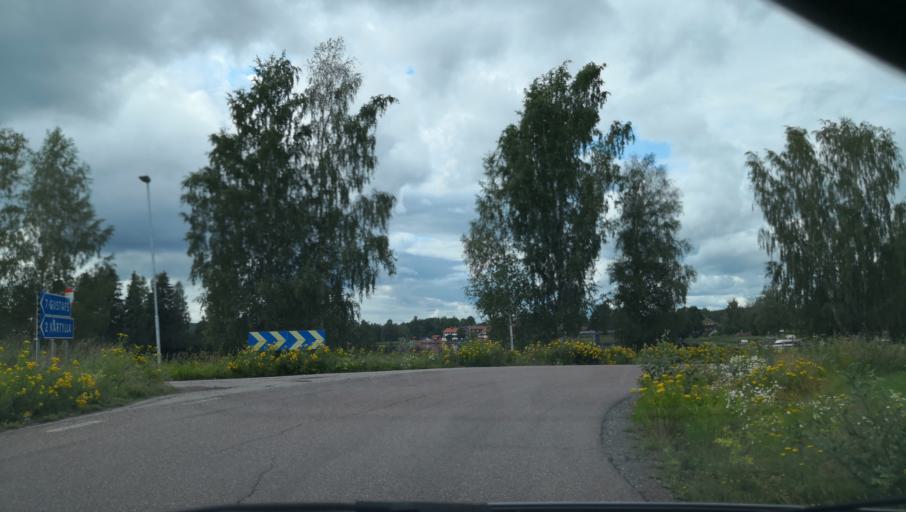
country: SE
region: Dalarna
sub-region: Borlange Kommun
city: Ornas
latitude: 60.4597
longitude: 15.5764
